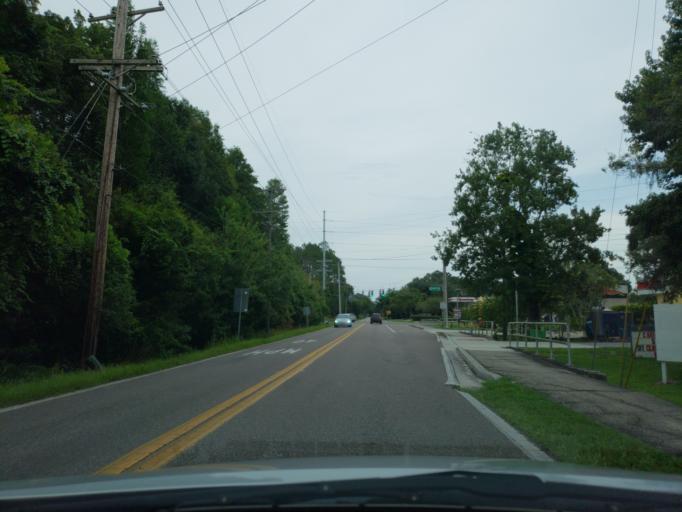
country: US
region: Florida
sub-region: Hillsborough County
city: Lutz
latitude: 28.1424
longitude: -82.4316
